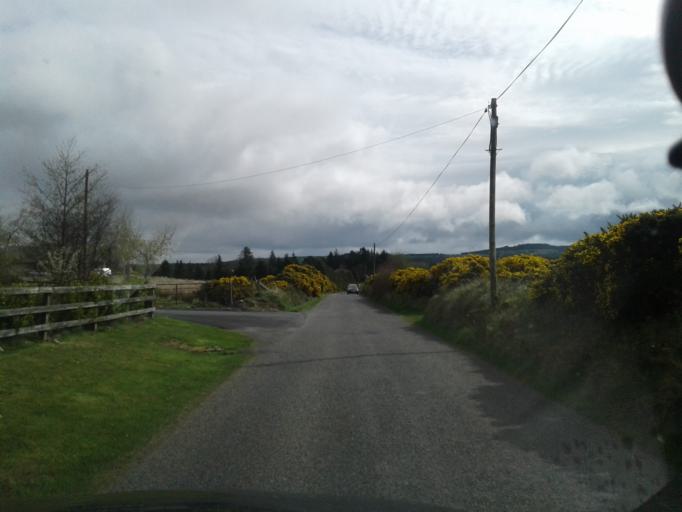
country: IE
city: Newtownmountkennedy
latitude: 53.0904
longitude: -6.2179
